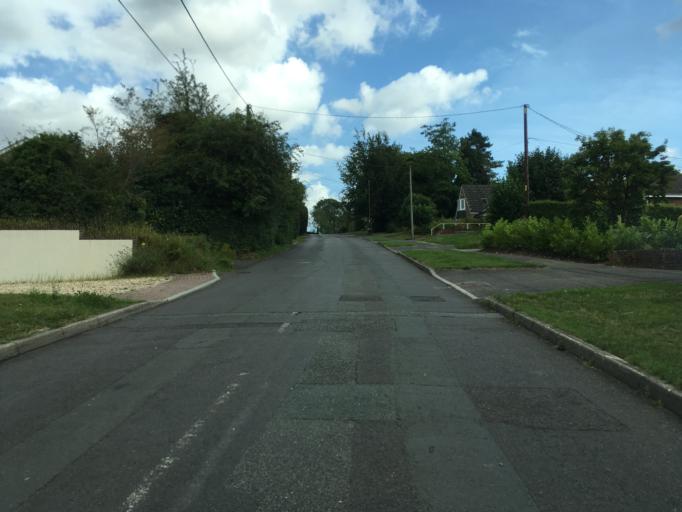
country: GB
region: England
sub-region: Hampshire
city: Kings Worthy
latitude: 51.0949
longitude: -1.3031
